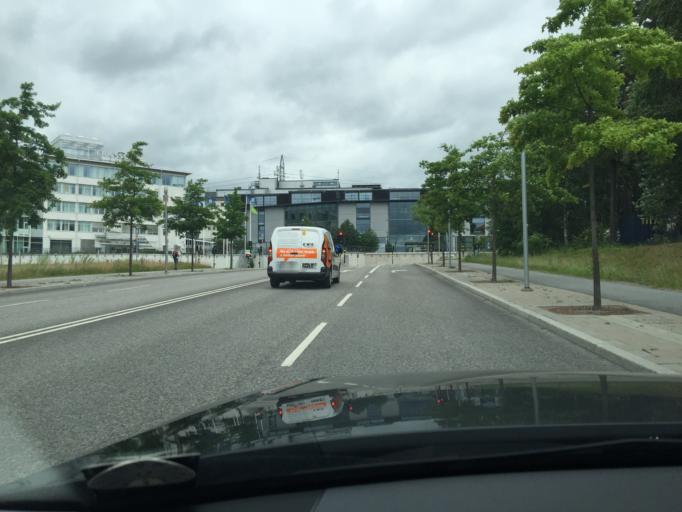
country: SE
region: Stockholm
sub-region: Stockholms Kommun
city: Kista
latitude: 59.4080
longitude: 17.9486
